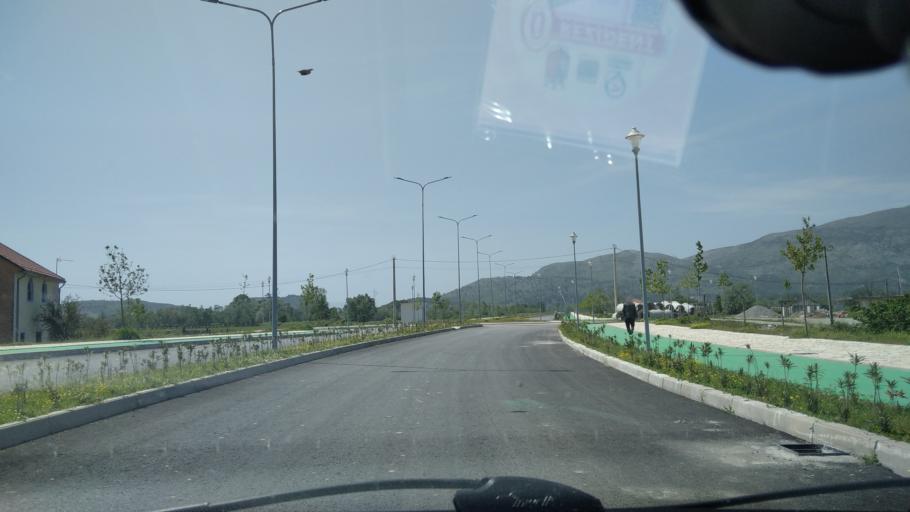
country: AL
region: Shkoder
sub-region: Rrethi i Shkodres
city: Shkoder
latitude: 42.0787
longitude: 19.4922
